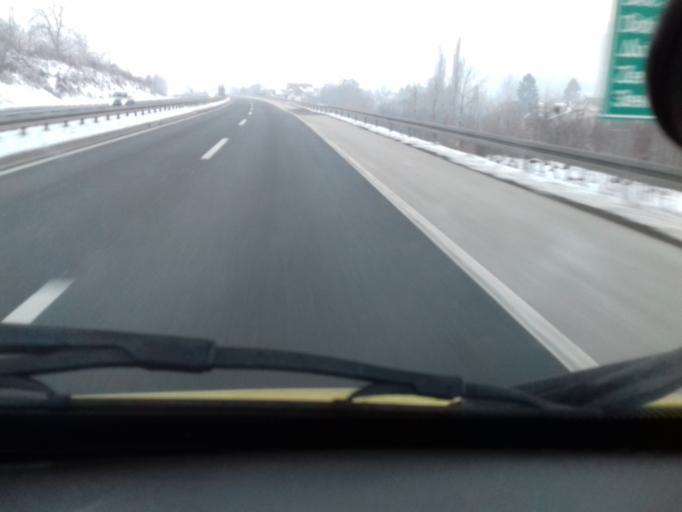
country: BA
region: Federation of Bosnia and Herzegovina
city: Vogosca
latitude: 43.9146
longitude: 18.3181
